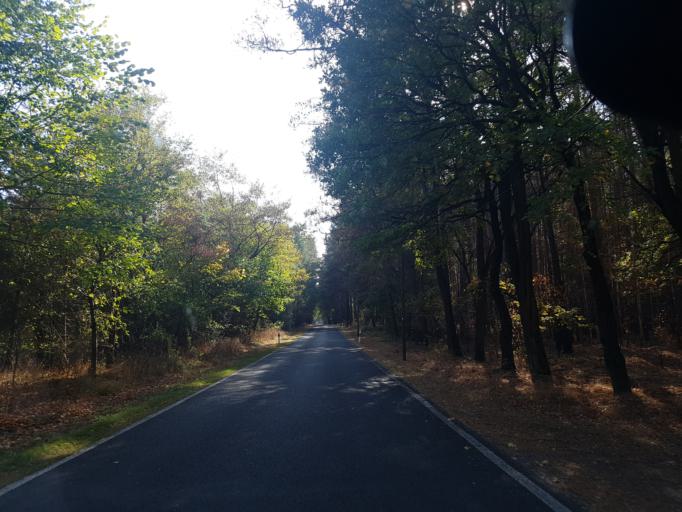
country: DE
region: Brandenburg
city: Lebusa
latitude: 51.8245
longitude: 13.3929
